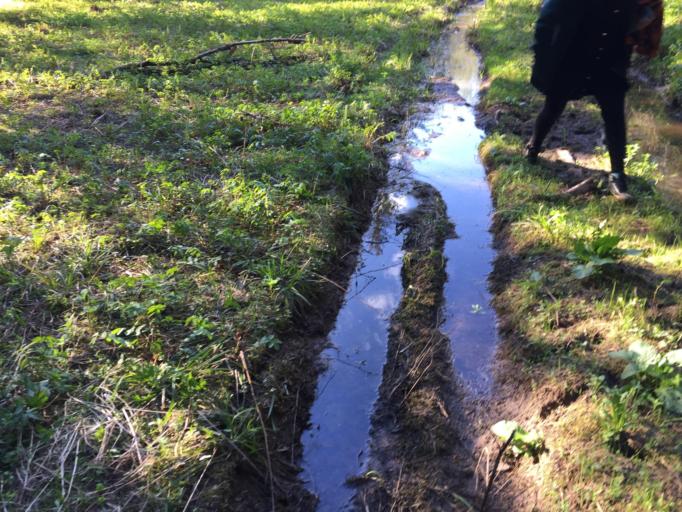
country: LV
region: Vecpiebalga
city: Vecpiebalga
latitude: 56.8690
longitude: 25.9547
